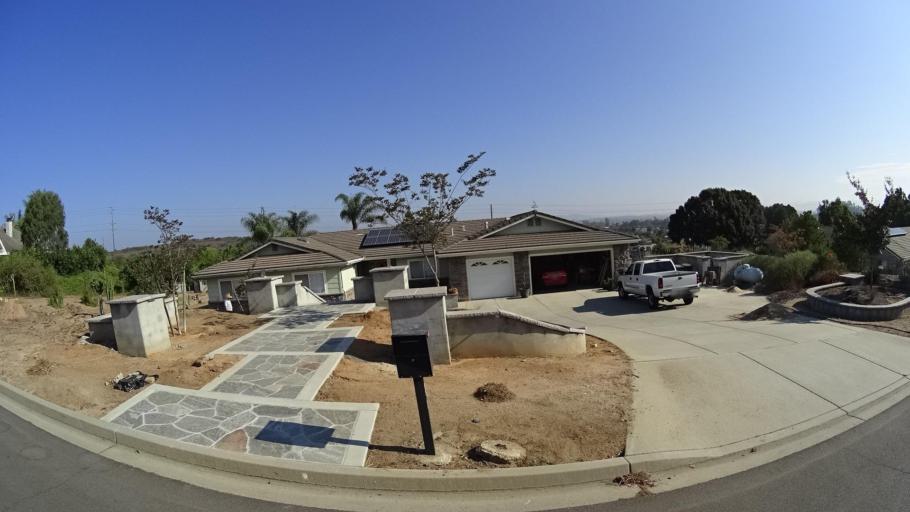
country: US
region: California
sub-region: San Diego County
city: Bonsall
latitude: 33.3285
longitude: -117.2507
